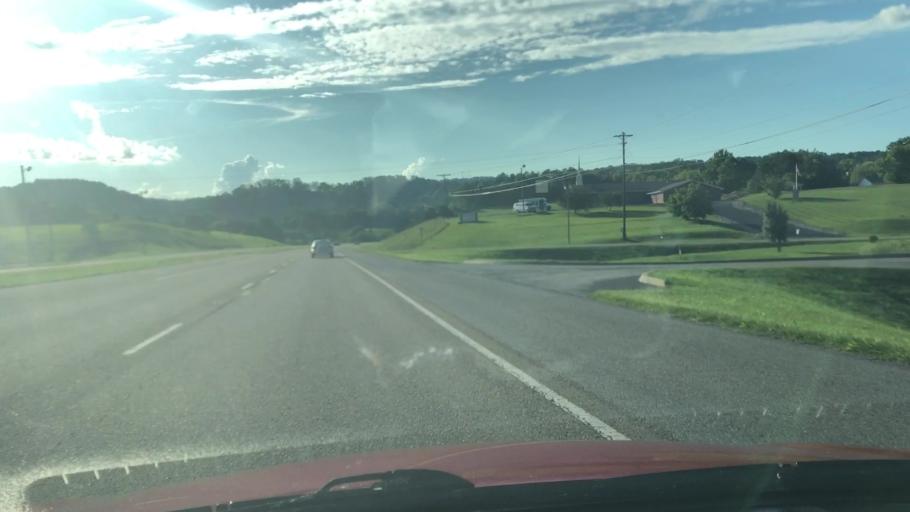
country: US
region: Tennessee
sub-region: Jefferson County
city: Dandridge
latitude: 36.0465
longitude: -83.4571
